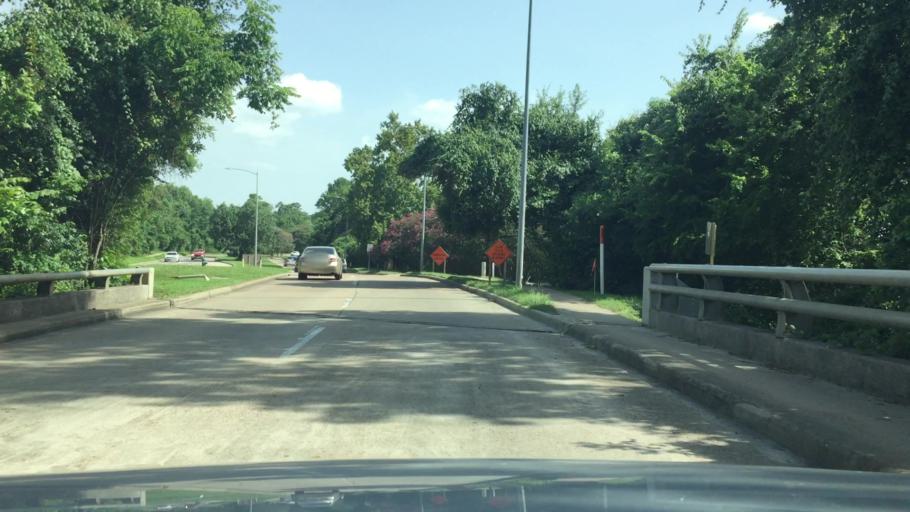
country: US
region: Texas
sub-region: Harris County
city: Bunker Hill Village
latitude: 29.7656
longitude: -95.5761
